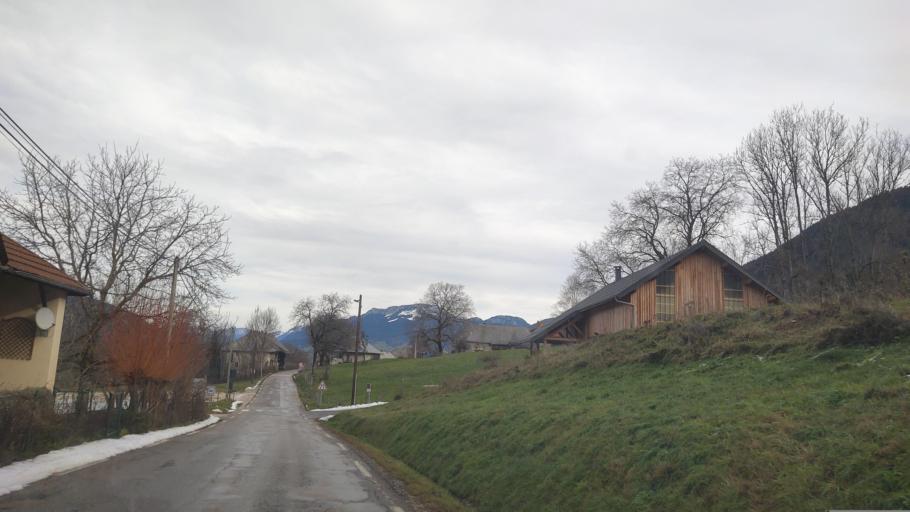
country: FR
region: Rhone-Alpes
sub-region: Departement de la Haute-Savoie
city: Cusy
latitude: 45.6798
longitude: 6.0623
